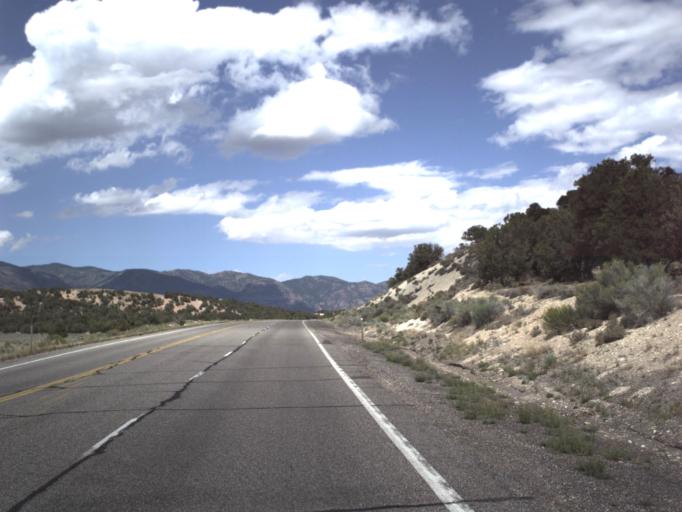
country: US
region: Utah
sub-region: Sevier County
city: Aurora
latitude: 38.9988
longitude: -112.0216
